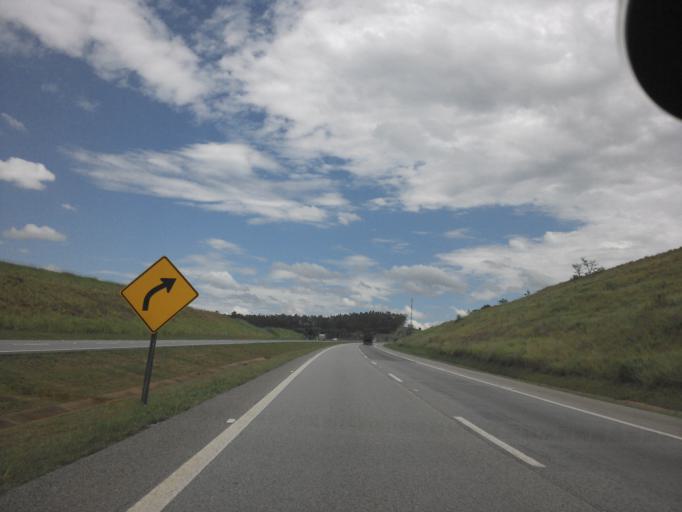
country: BR
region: Sao Paulo
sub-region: Cacapava
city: Cacapava
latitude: -23.1288
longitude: -45.6568
